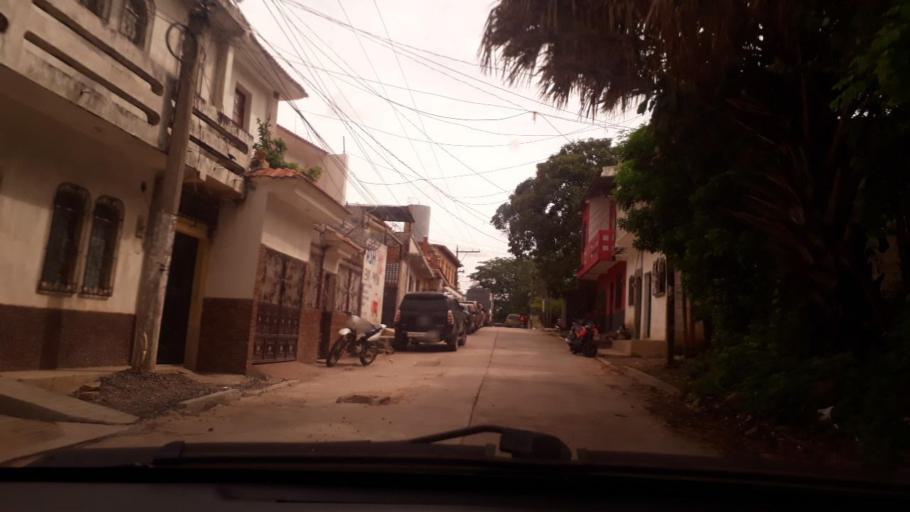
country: GT
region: Jutiapa
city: Jutiapa
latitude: 14.3012
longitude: -89.8907
